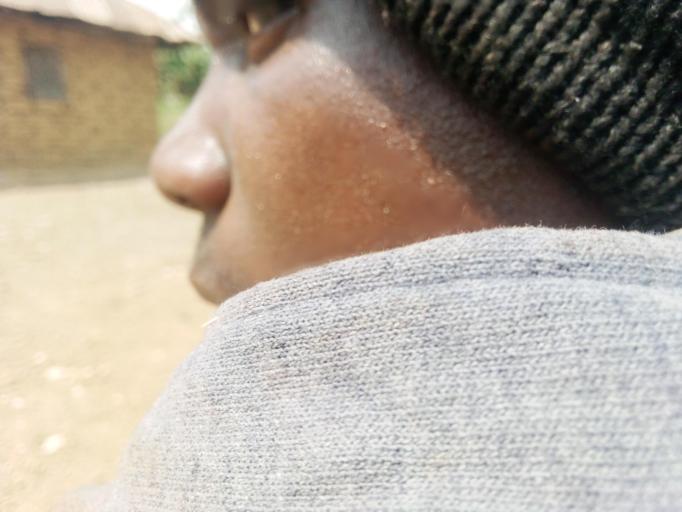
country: SL
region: Southern Province
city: Mogbwemo
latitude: 7.6114
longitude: -12.1864
